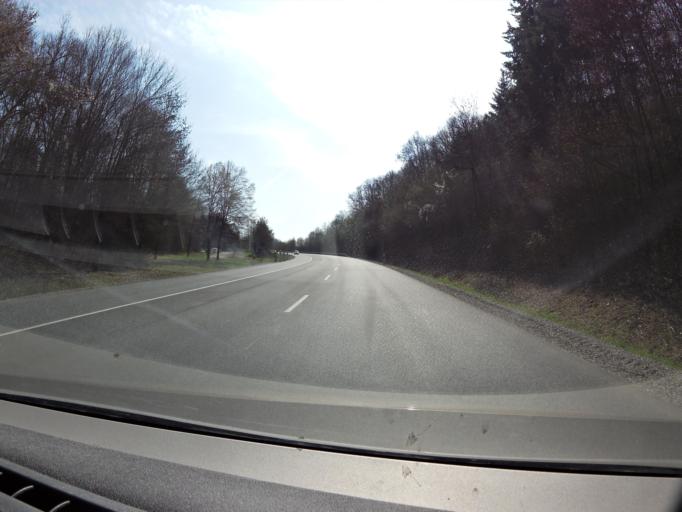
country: DE
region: Bavaria
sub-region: Regierungsbezirk Unterfranken
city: Ochsenfurt
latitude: 49.6565
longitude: 10.0721
